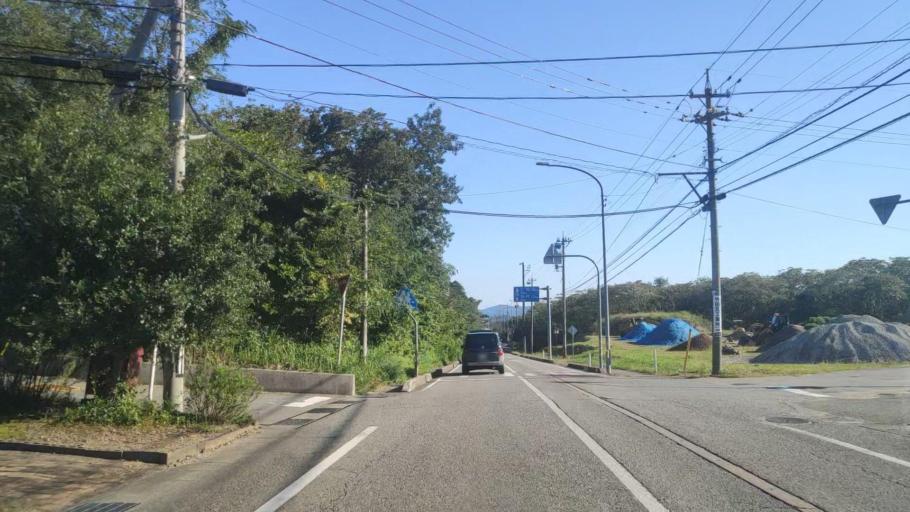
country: JP
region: Ishikawa
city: Tsubata
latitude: 36.7807
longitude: 136.7360
